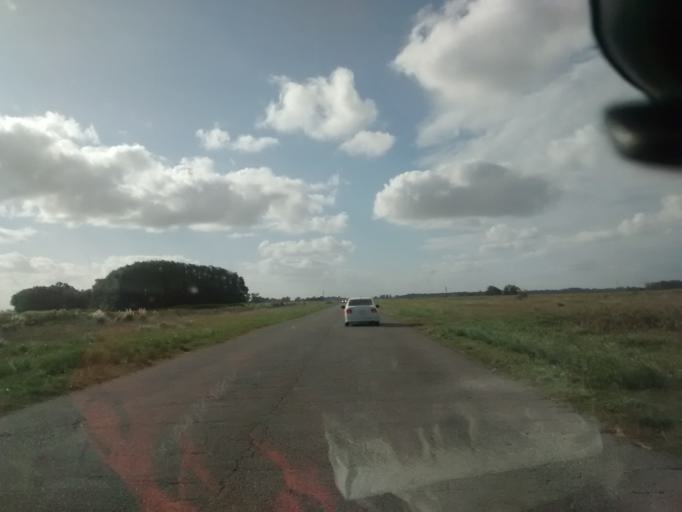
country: AR
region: Buenos Aires
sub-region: Partido de Ayacucho
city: Ayacucho
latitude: -37.2029
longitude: -58.5057
